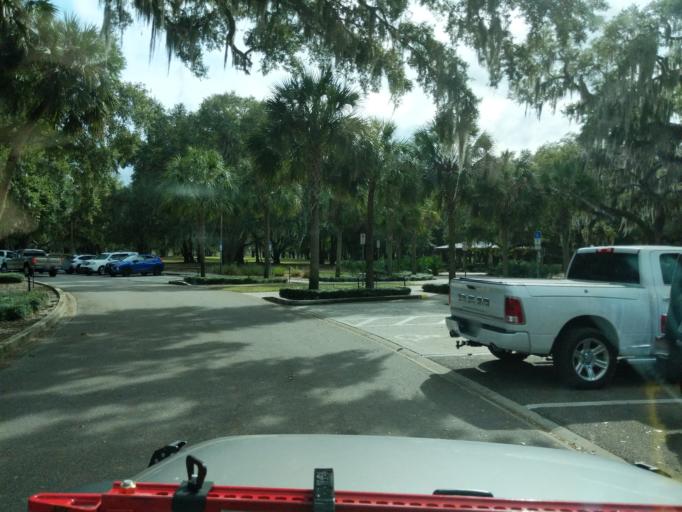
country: US
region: Florida
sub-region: Lake County
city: Clermont
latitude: 28.5703
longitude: -81.7806
